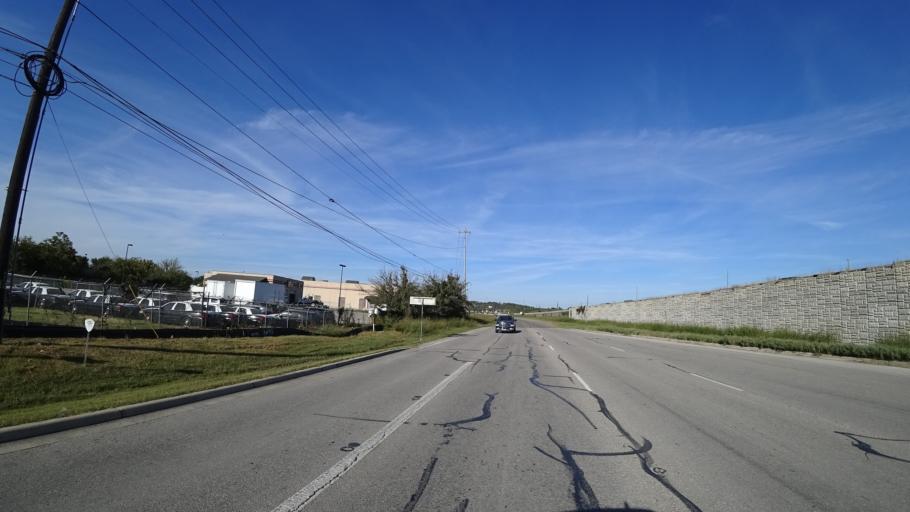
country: US
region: Texas
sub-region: Travis County
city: Austin
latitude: 30.2543
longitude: -97.6793
